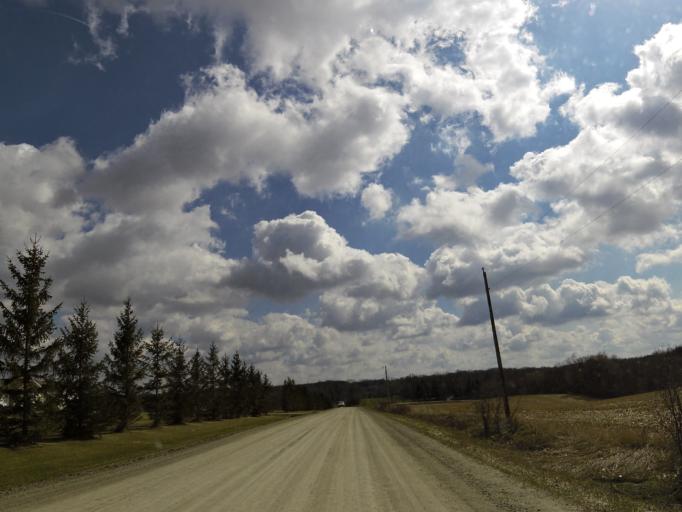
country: US
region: Minnesota
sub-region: Dodge County
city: Mantorville
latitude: 44.0719
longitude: -92.7182
